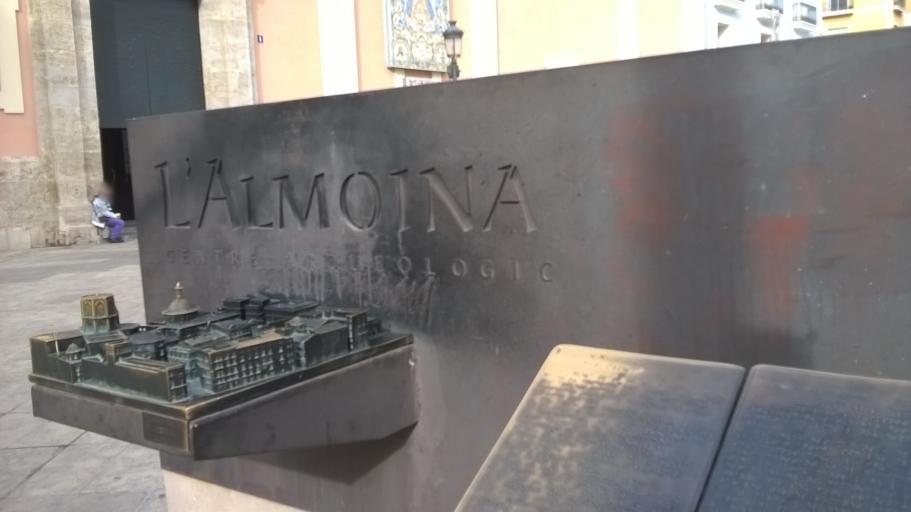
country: ES
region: Valencia
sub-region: Provincia de Valencia
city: Valencia
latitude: 39.4758
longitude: -0.3745
